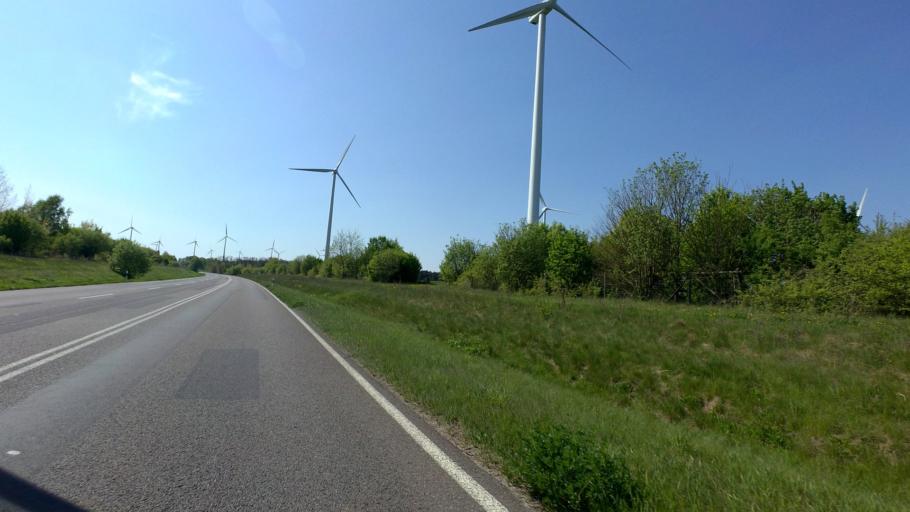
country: DE
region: Brandenburg
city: Beeskow
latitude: 52.2004
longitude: 14.2451
